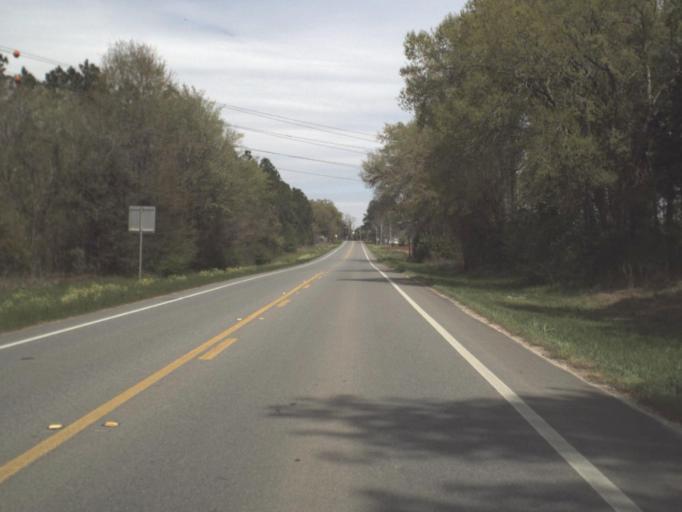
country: US
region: Florida
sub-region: Jackson County
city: Graceville
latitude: 30.9446
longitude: -85.4074
